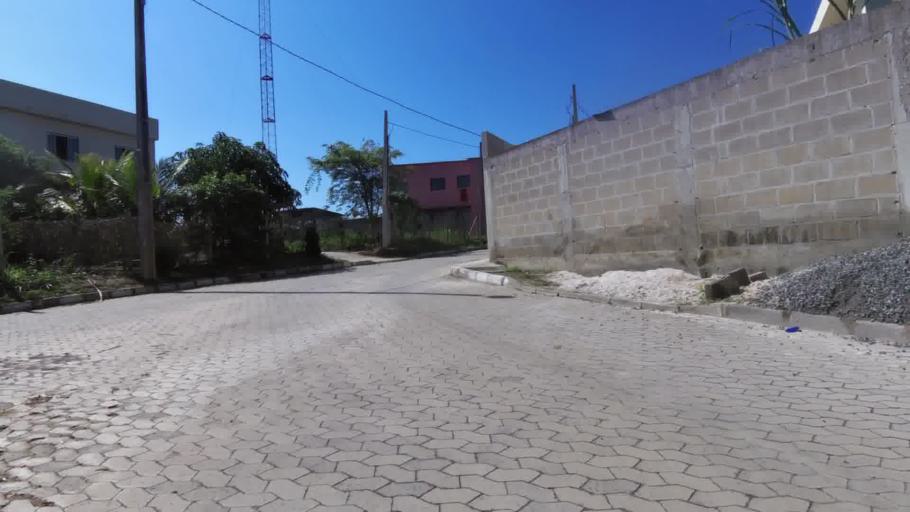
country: BR
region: Espirito Santo
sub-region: Piuma
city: Piuma
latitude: -20.8277
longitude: -40.6275
